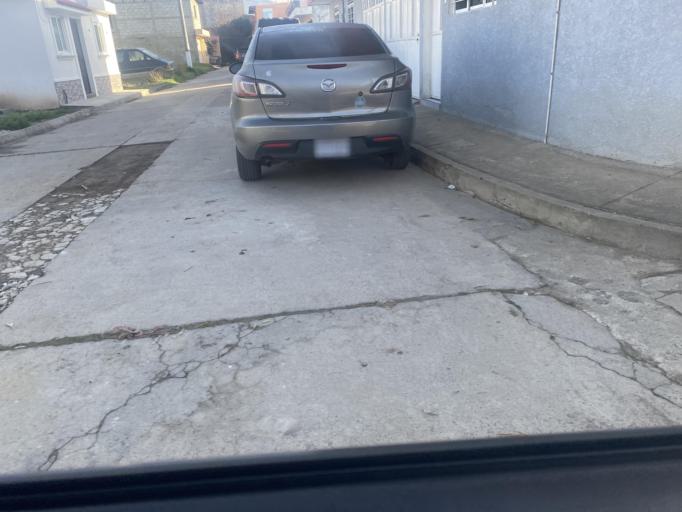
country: GT
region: Quetzaltenango
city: Olintepeque
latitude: 14.8685
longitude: -91.5196
